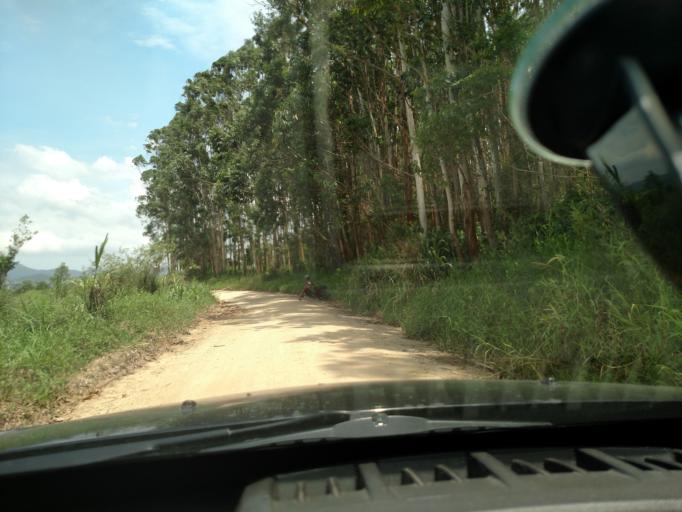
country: BR
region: Santa Catarina
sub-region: Itajai
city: Itajai
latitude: -26.9634
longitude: -48.7994
